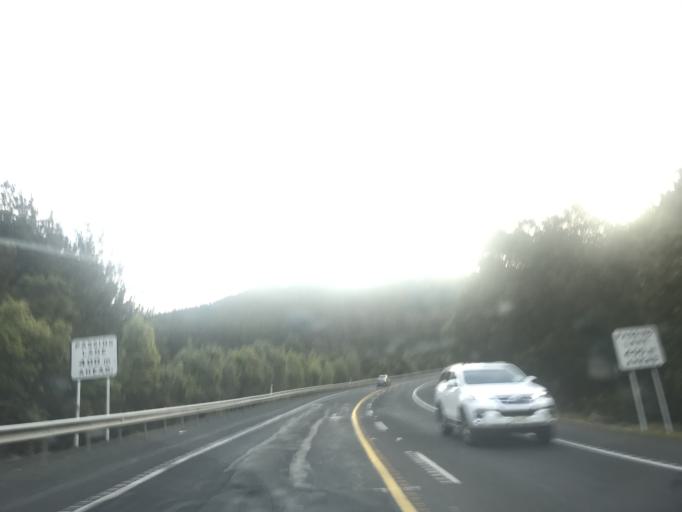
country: NZ
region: Bay of Plenty
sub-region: Western Bay of Plenty District
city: Waihi Beach
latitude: -37.4629
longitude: 175.9158
